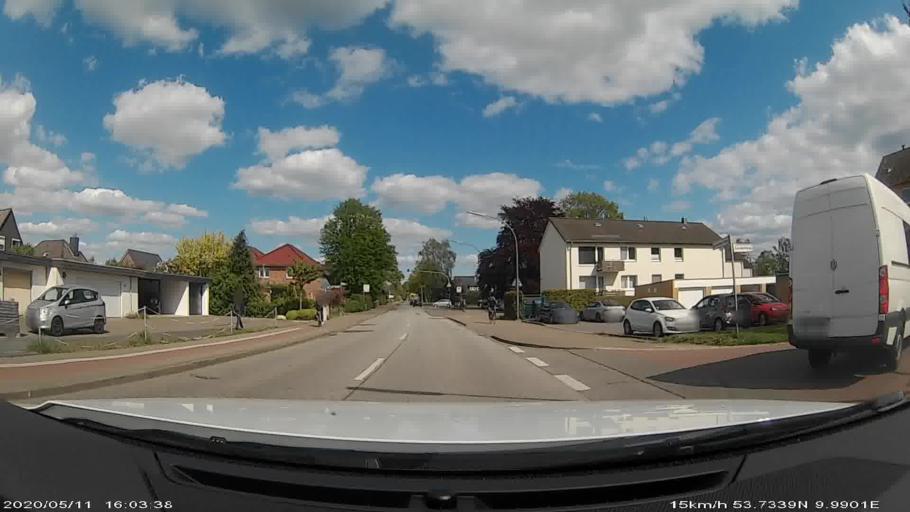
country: DE
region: Schleswig-Holstein
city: Norderstedt
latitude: 53.7358
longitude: 9.9965
